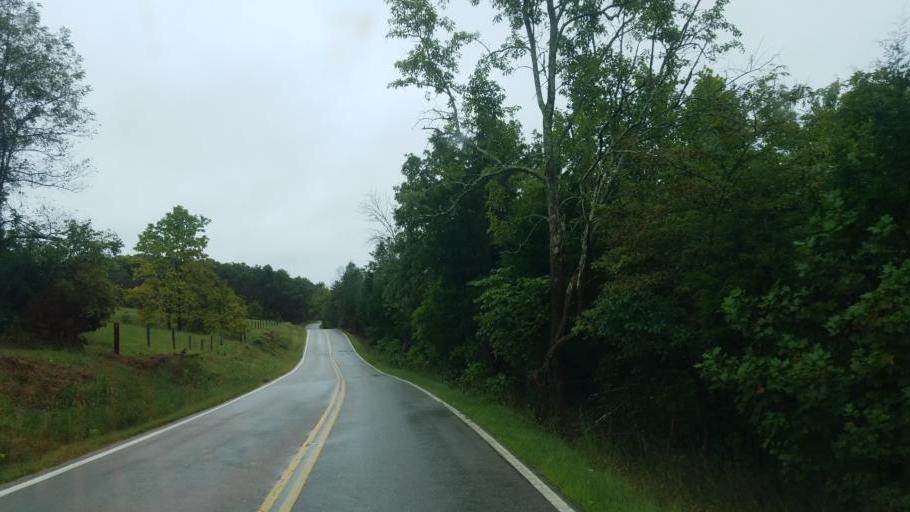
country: US
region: Ohio
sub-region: Adams County
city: West Union
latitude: 38.7837
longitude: -83.5383
